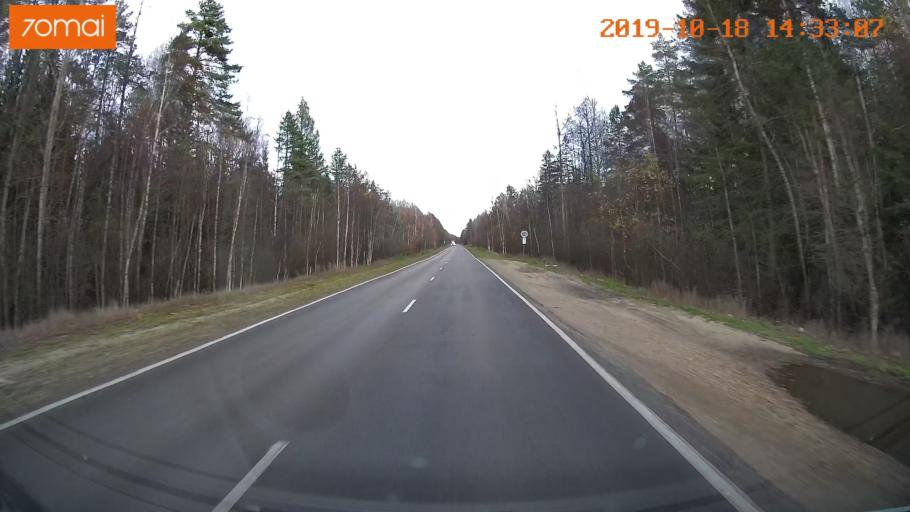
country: RU
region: Rjazan
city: Tuma
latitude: 55.1978
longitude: 40.5908
